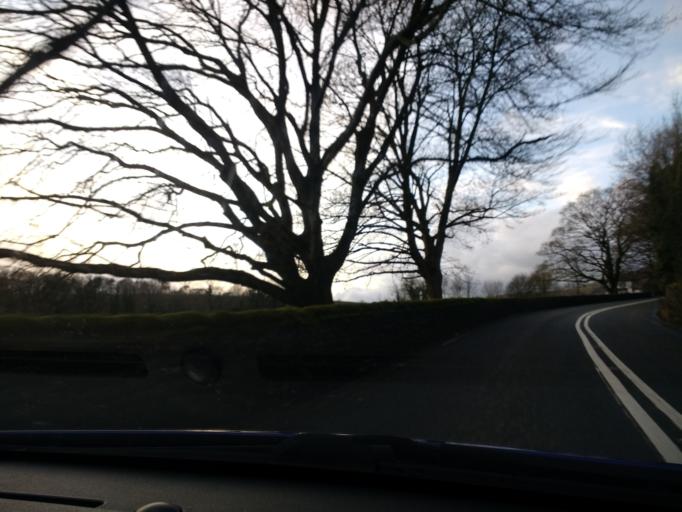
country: GB
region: England
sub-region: North Yorkshire
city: Settle
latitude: 54.0770
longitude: -2.2933
